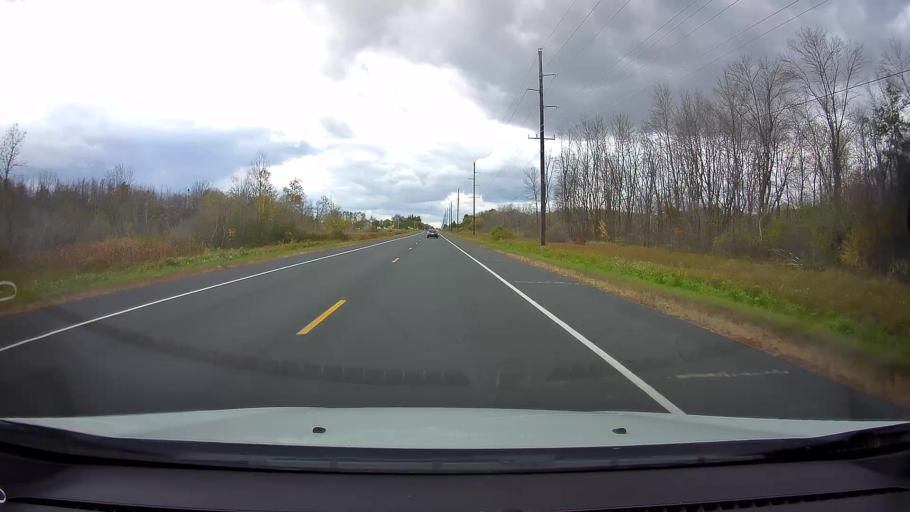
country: US
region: Minnesota
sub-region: Chisago County
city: Shafer
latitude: 45.3972
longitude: -92.7595
